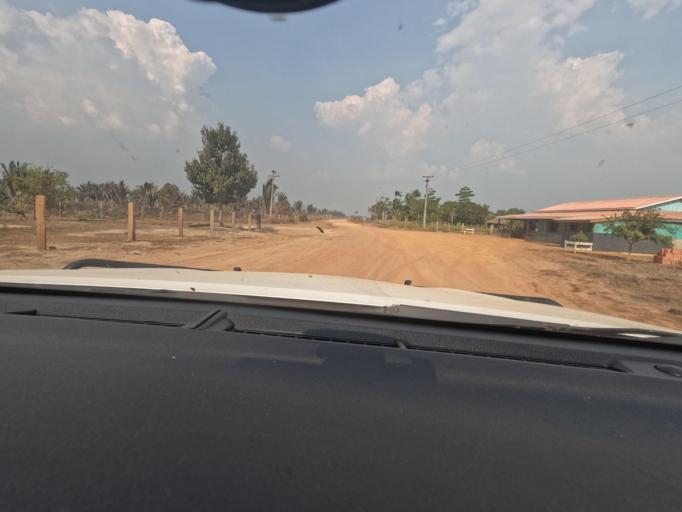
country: BR
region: Rondonia
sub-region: Porto Velho
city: Porto Velho
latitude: -8.6831
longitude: -63.1559
